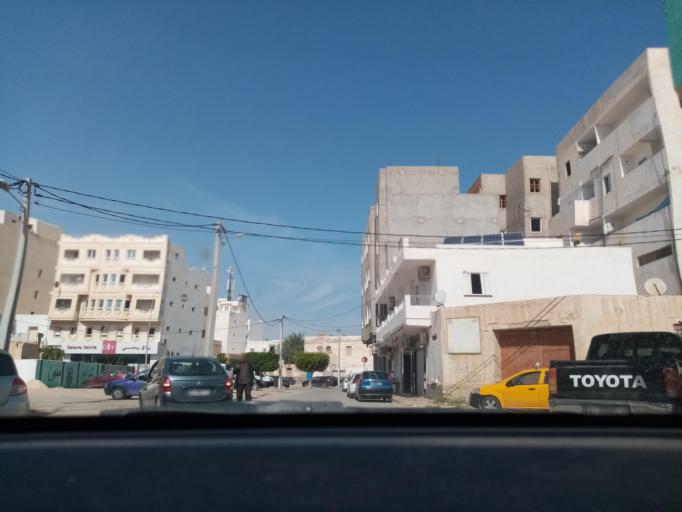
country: TN
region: Qabis
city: Gabes
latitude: 33.8859
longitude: 10.1047
